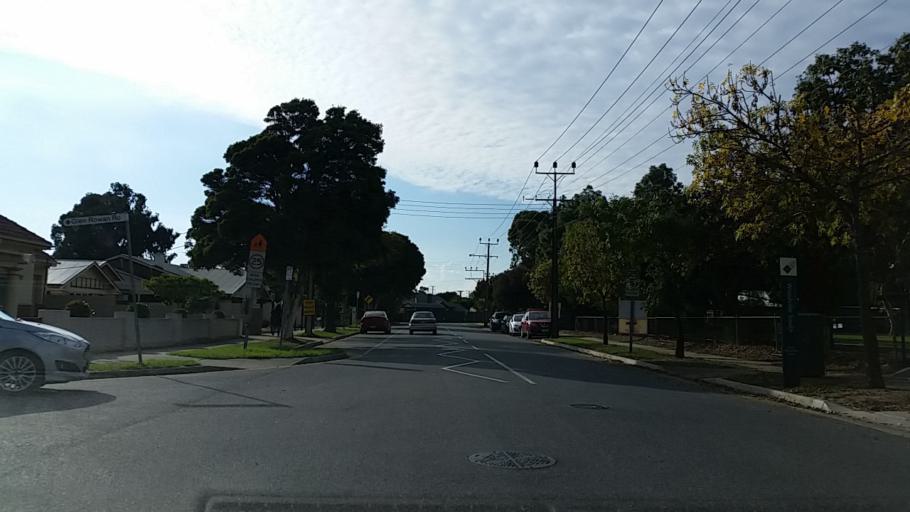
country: AU
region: South Australia
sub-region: Charles Sturt
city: Woodville West
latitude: -34.8858
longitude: 138.5371
